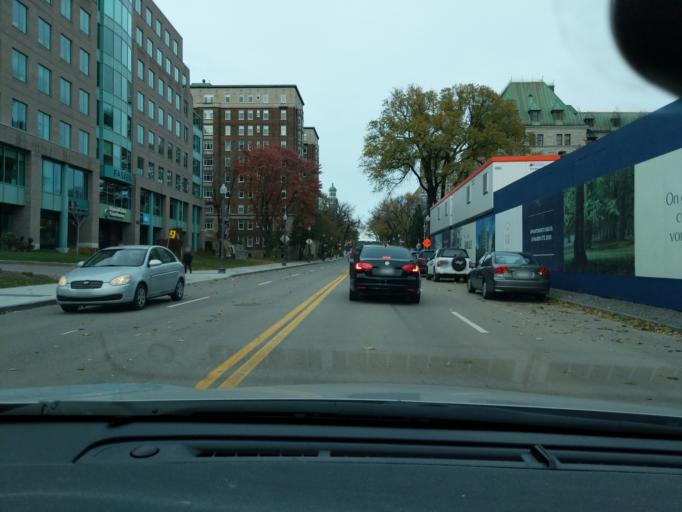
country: CA
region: Quebec
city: Quebec
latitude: 46.8030
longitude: -71.2222
